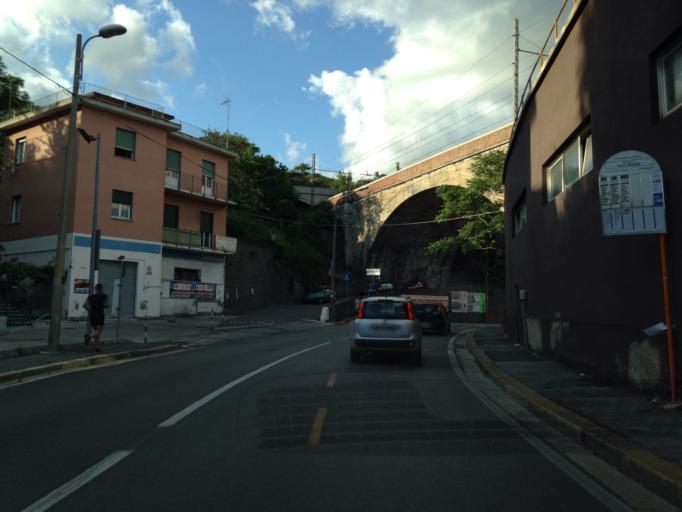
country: IT
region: Liguria
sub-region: Provincia di Genova
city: Genoa
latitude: 44.4419
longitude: 8.8876
